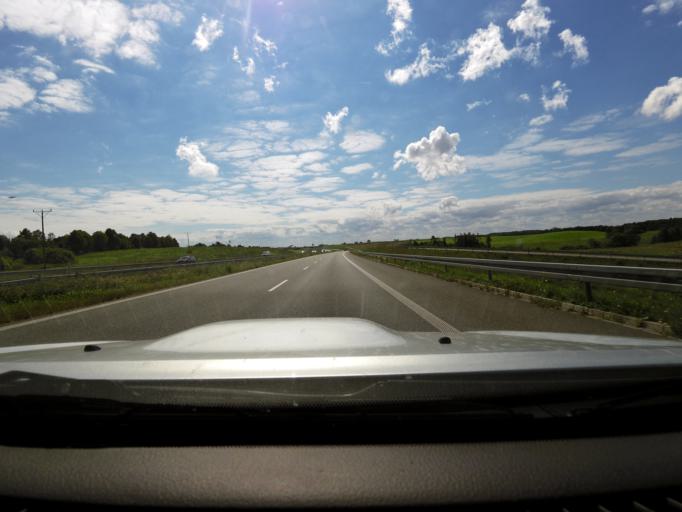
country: PL
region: Warmian-Masurian Voivodeship
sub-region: Powiat ostrodzki
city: Maldyty
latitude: 53.8567
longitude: 19.7498
